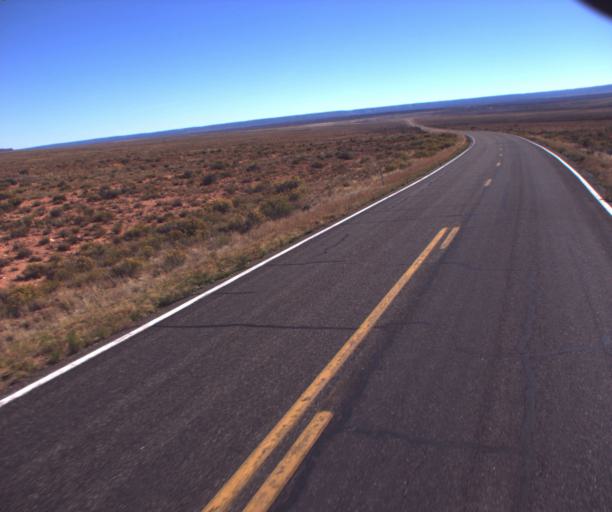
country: US
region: Arizona
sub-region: Coconino County
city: Fredonia
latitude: 36.9291
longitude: -112.4884
